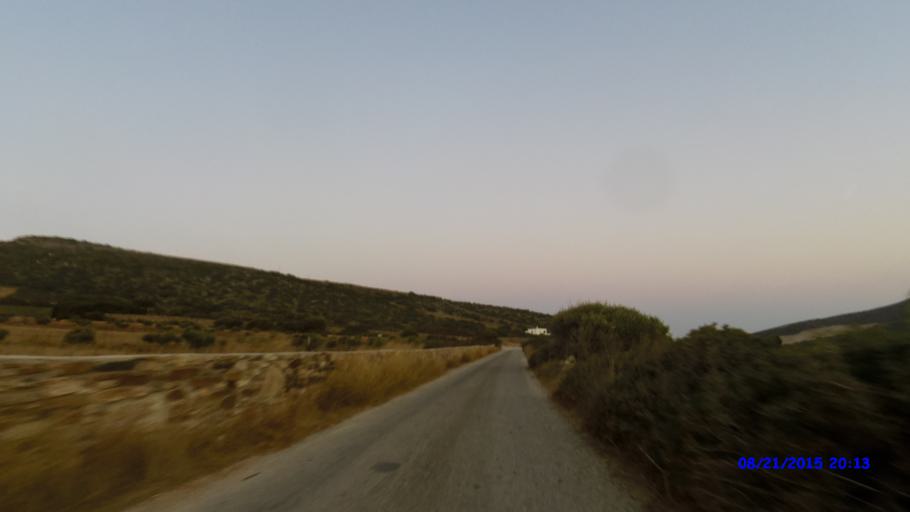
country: GR
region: South Aegean
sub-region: Nomos Kykladon
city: Antiparos
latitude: 37.0144
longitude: 25.0624
